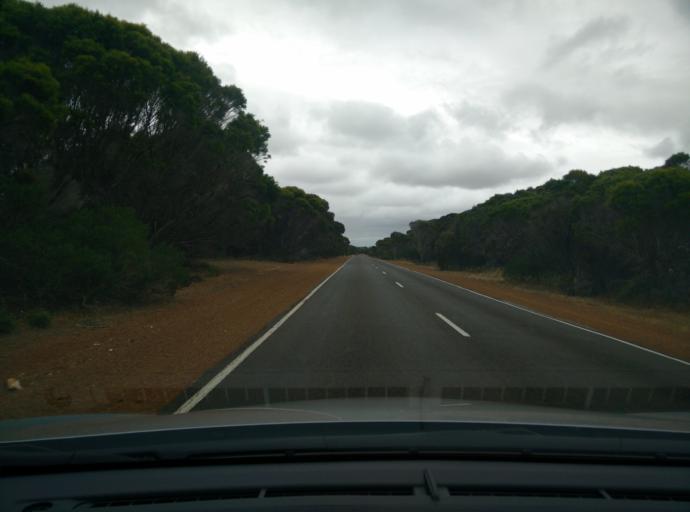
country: AU
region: South Australia
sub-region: Kangaroo Island
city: Kingscote
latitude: -35.7115
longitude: 137.5634
